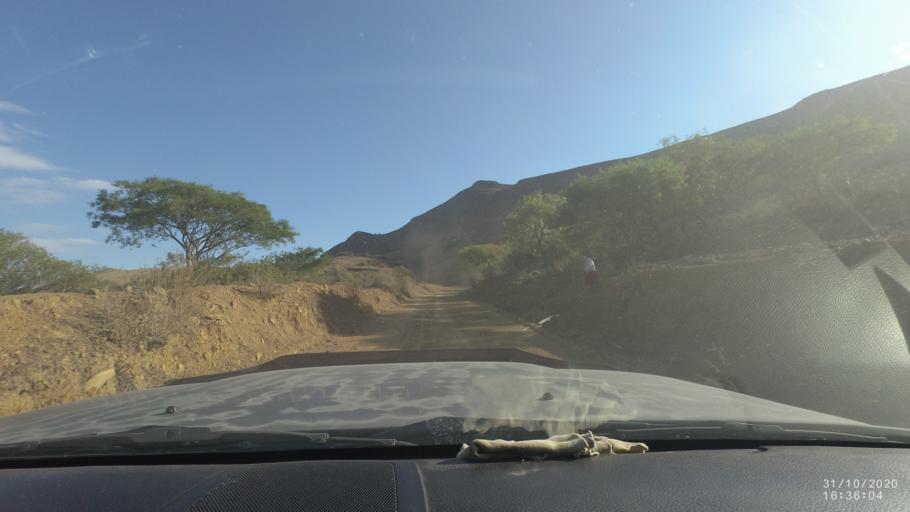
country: BO
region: Chuquisaca
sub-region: Provincia Zudanez
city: Mojocoya
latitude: -18.4571
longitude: -64.5824
